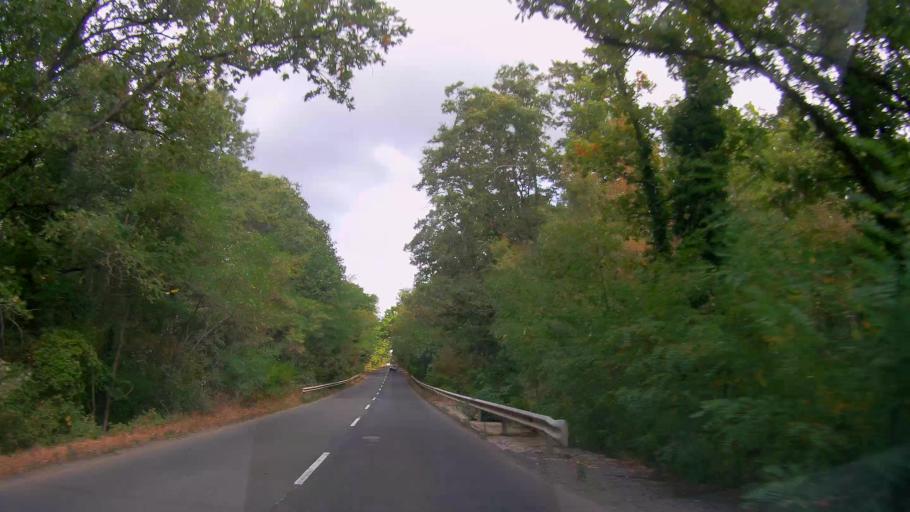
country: BG
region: Burgas
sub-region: Obshtina Primorsko
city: Primorsko
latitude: 42.2860
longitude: 27.7364
